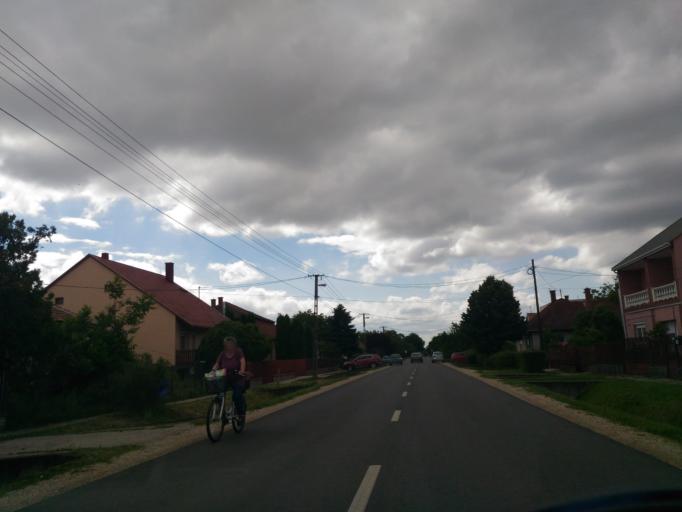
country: HU
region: Fejer
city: Pusztaszabolcs
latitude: 47.1423
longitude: 18.7555
